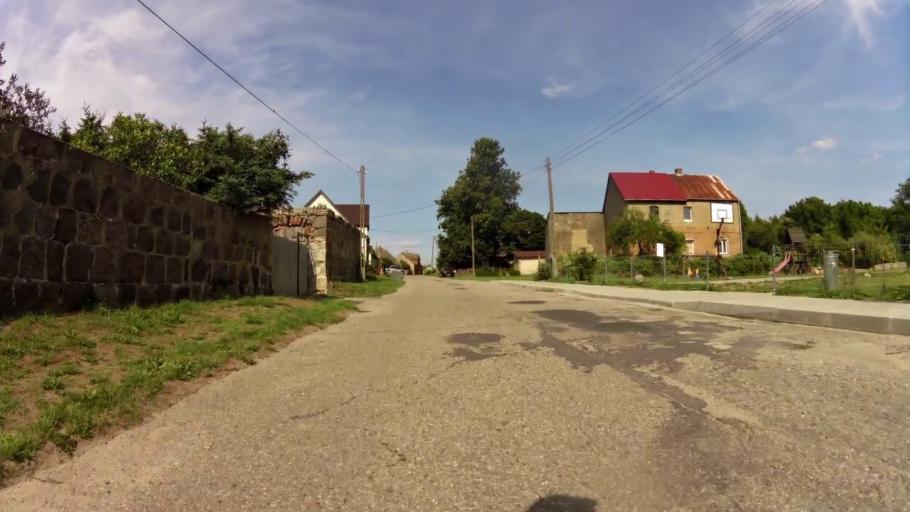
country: PL
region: West Pomeranian Voivodeship
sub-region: Powiat stargardzki
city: Insko
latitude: 53.3754
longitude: 15.5918
